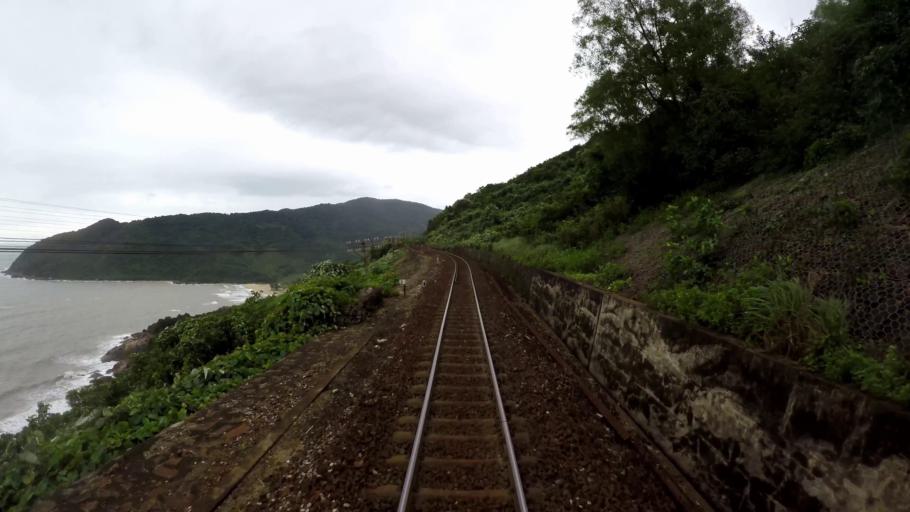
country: VN
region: Da Nang
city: Lien Chieu
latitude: 16.2143
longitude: 108.1322
